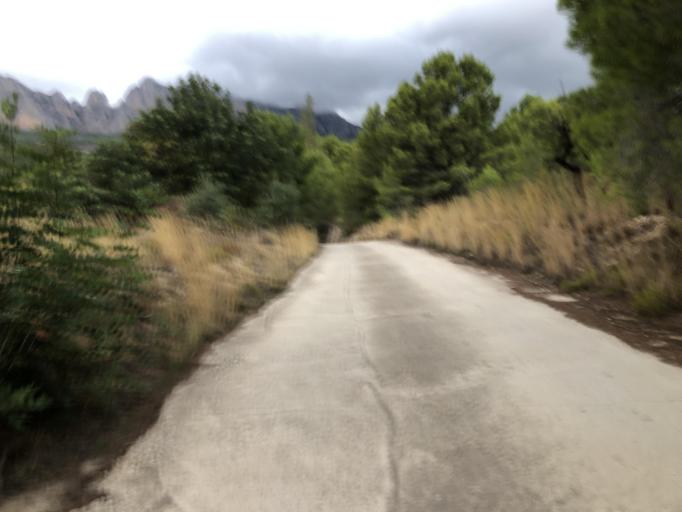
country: ES
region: Valencia
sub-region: Provincia de Alicante
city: Polop
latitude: 38.6370
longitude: -0.1544
